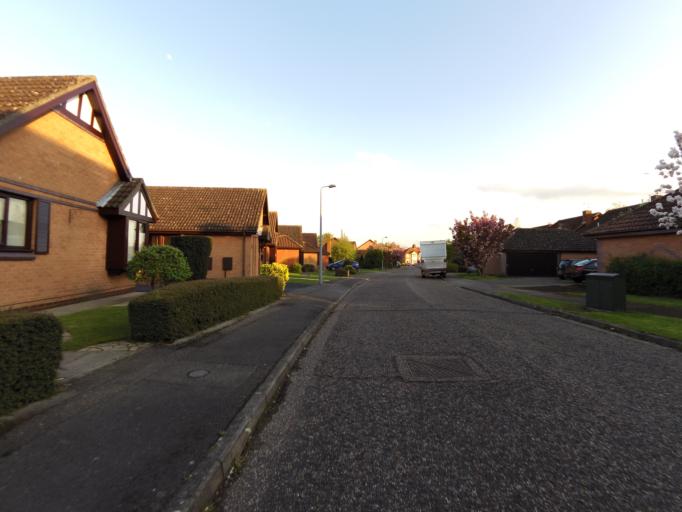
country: GB
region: England
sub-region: Suffolk
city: Ipswich
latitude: 52.0732
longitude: 1.1831
